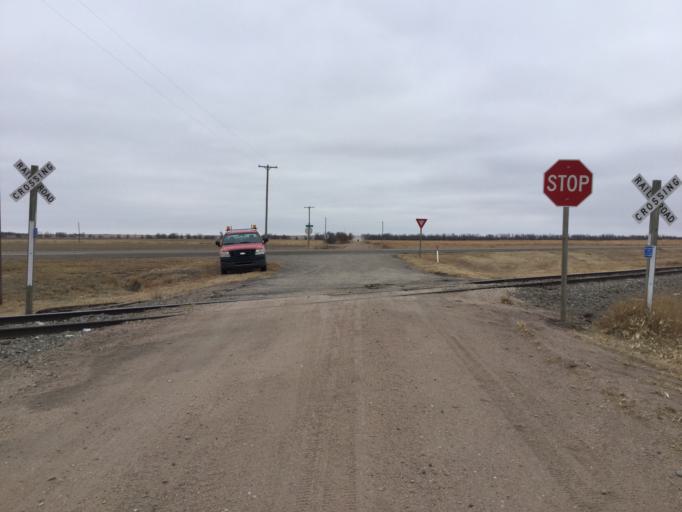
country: US
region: Kansas
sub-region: Pawnee County
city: Larned
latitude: 38.2380
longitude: -99.0223
